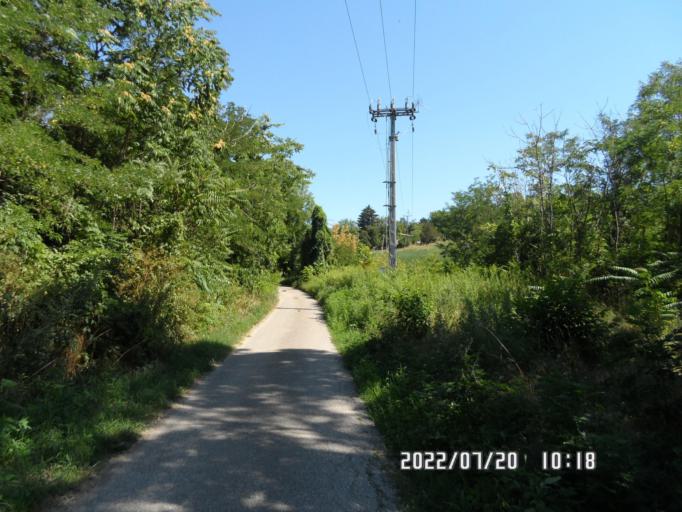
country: HU
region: Somogy
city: Siofok
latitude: 46.8484
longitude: 18.0226
